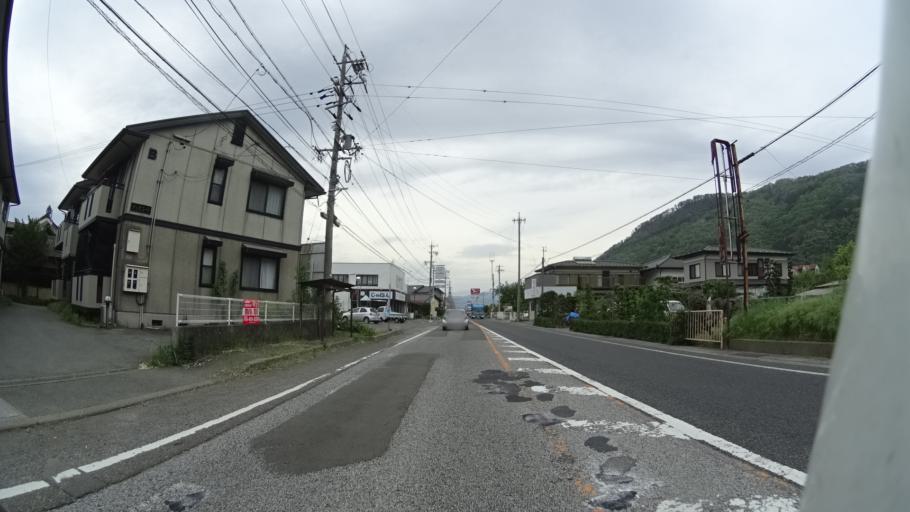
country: JP
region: Nagano
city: Nagano-shi
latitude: 36.5076
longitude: 138.1399
